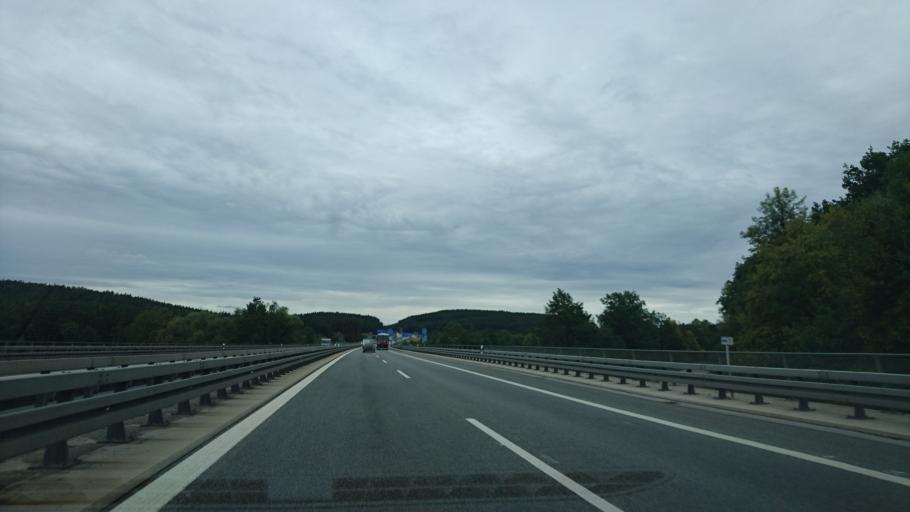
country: DE
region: Bavaria
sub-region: Upper Palatinate
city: Pfreimd
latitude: 49.5114
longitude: 12.1722
